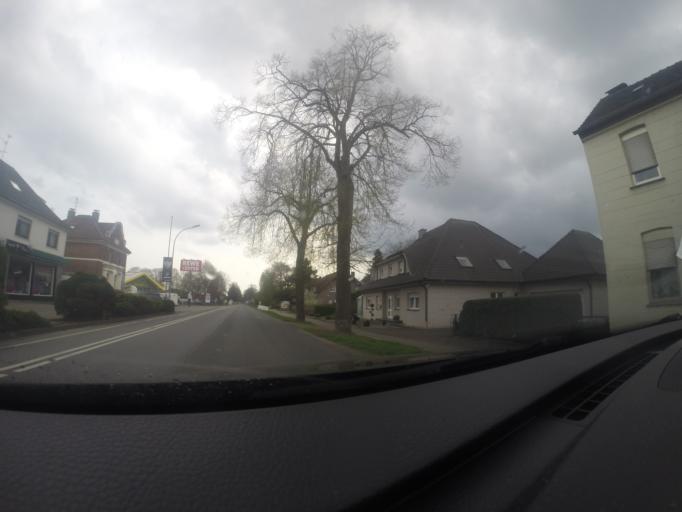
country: DE
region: North Rhine-Westphalia
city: Rheinberg
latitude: 51.5415
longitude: 6.6058
